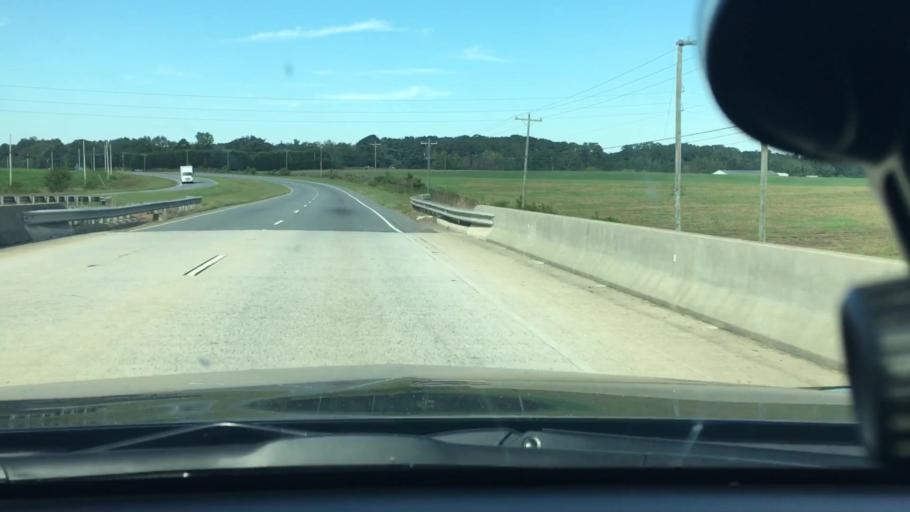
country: US
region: North Carolina
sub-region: Cabarrus County
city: Midland
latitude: 35.2552
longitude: -80.4738
